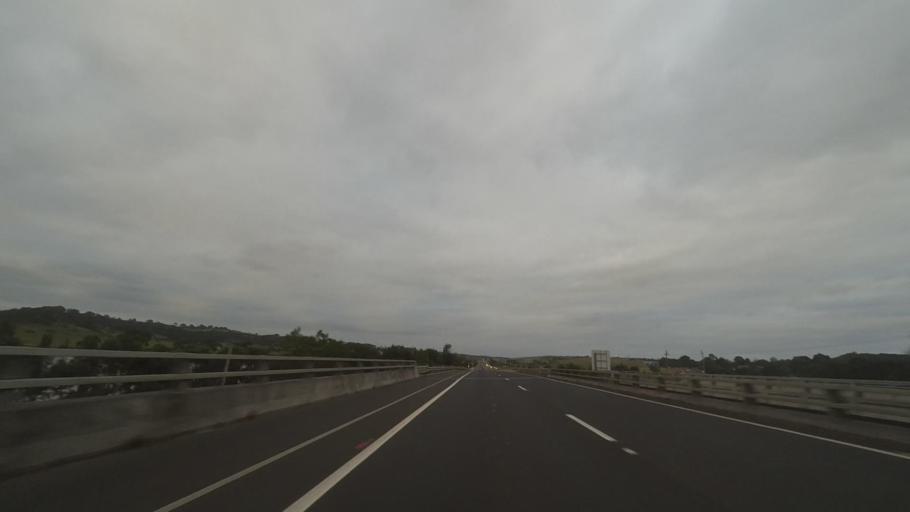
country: AU
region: New South Wales
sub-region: Shellharbour
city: Croom
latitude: -34.6086
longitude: 150.8381
